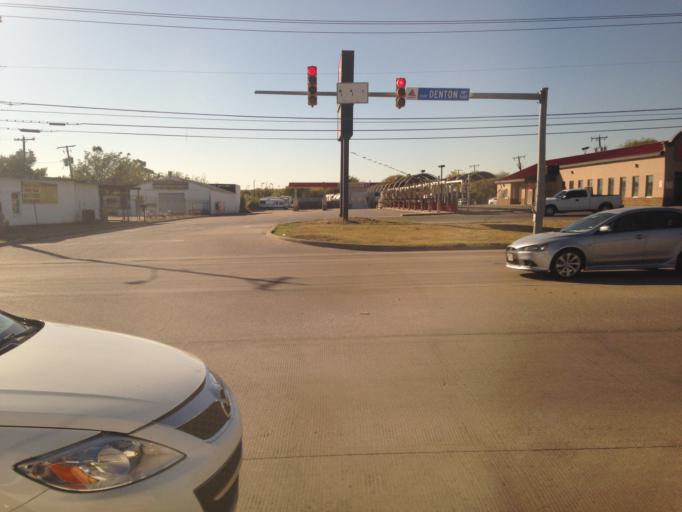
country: US
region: Texas
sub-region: Tarrant County
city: Watauga
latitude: 32.8478
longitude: -97.2639
